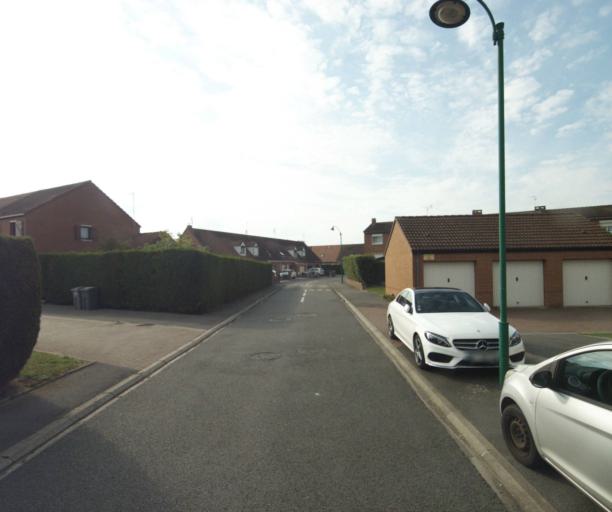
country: FR
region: Nord-Pas-de-Calais
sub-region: Departement du Nord
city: Hallennes-lez-Haubourdin
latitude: 50.6118
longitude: 2.9614
